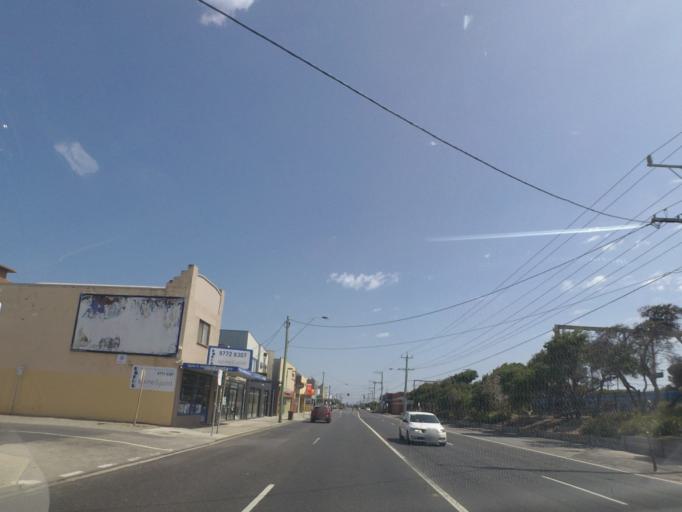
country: AU
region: Victoria
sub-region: Kingston
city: Bonbeach
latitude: -38.0763
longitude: 145.1224
